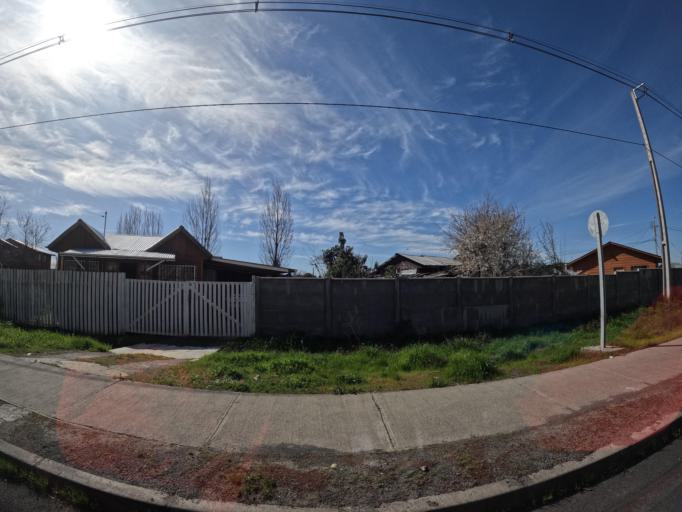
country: CL
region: Biobio
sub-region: Provincia de Biobio
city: Cabrero
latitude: -37.0383
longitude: -72.4069
